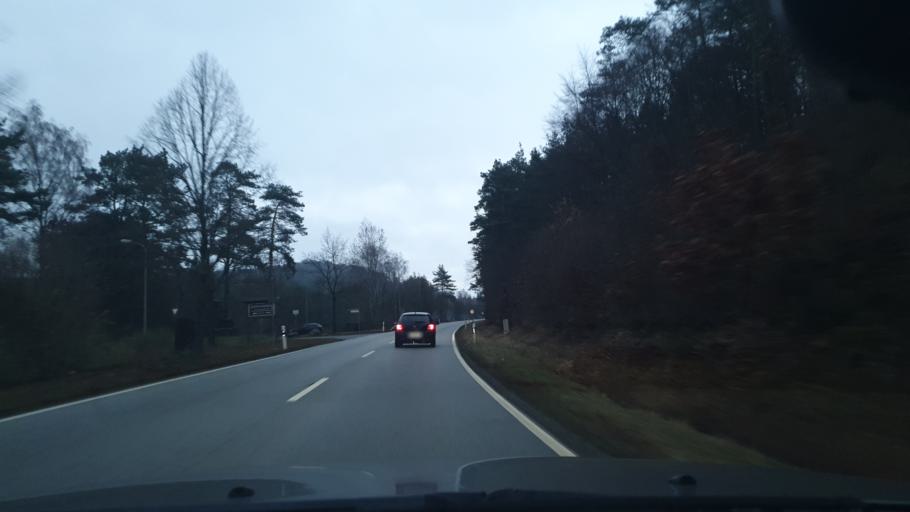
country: DE
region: Rheinland-Pfalz
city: Queidersbach
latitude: 49.3804
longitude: 7.6426
